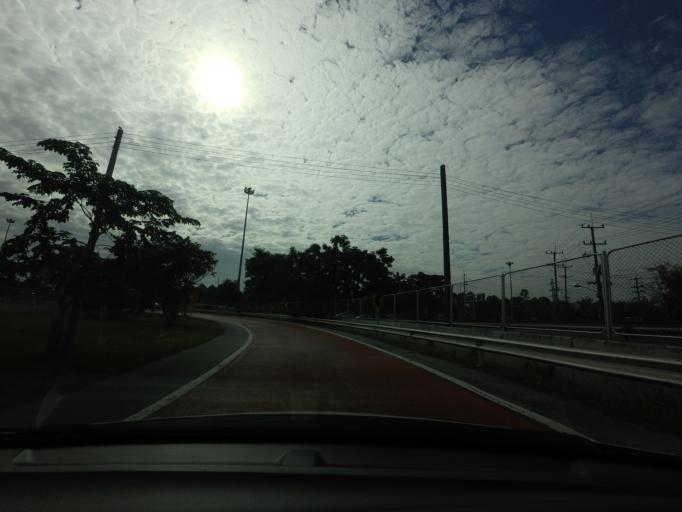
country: TH
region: Pathum Thani
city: Thanyaburi
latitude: 14.0078
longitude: 100.7028
